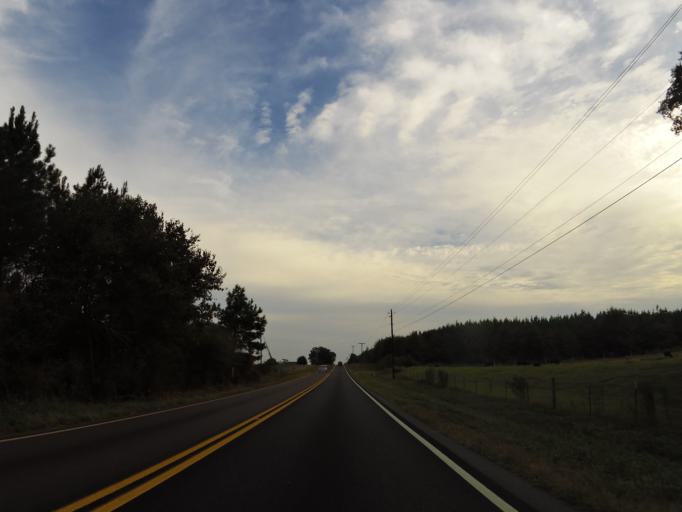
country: US
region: Alabama
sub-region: Escambia County
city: Atmore
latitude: 31.1883
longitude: -87.4638
